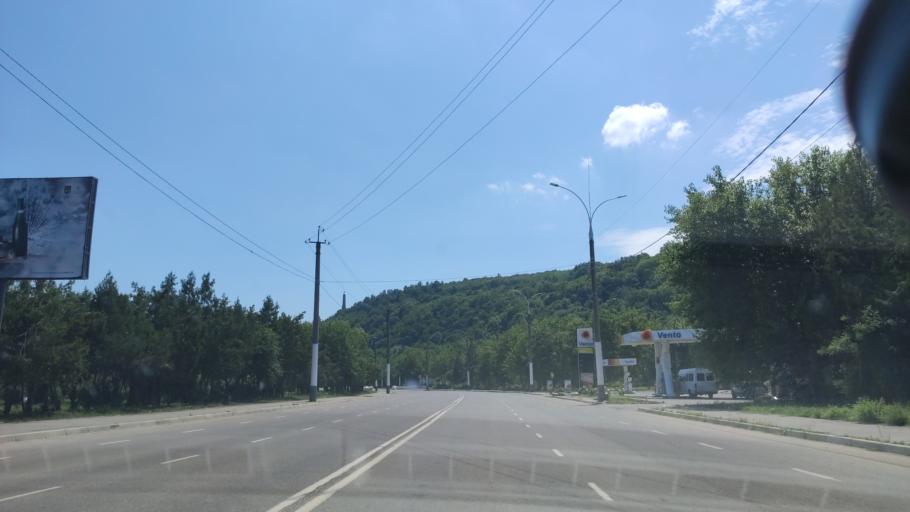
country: MD
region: Raionul Soroca
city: Soroca
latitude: 48.1451
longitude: 28.3021
